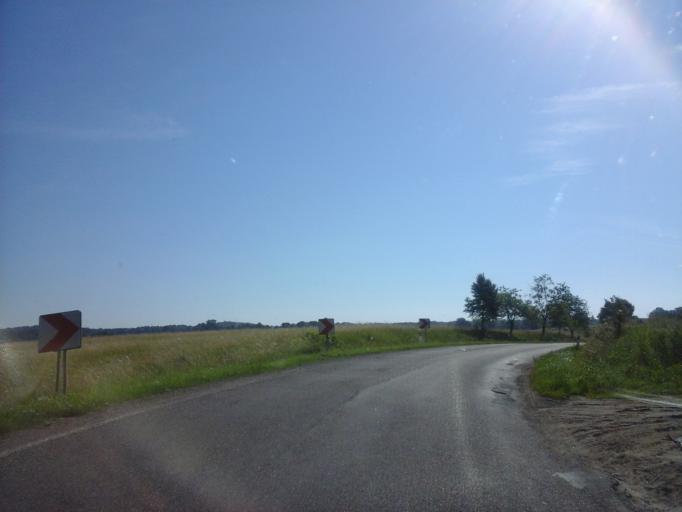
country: PL
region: West Pomeranian Voivodeship
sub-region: Powiat drawski
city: Zlocieniec
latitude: 53.6399
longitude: 15.9897
